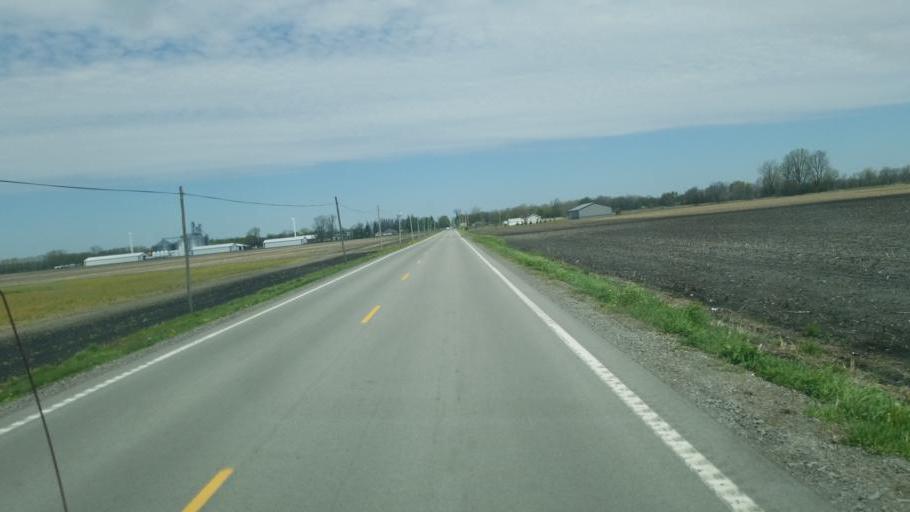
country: US
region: Ohio
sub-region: Hardin County
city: Ada
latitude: 40.6809
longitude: -83.7854
